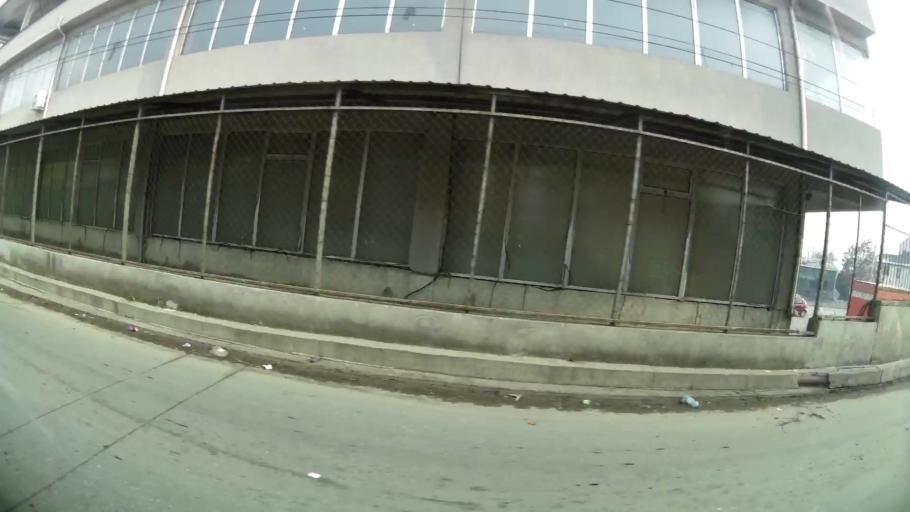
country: MK
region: Cair
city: Cair
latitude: 42.0119
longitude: 21.4316
